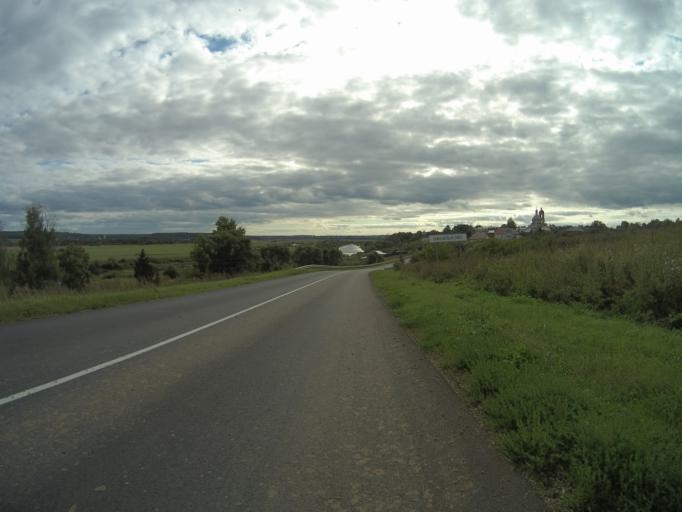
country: RU
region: Vladimir
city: Bogolyubovo
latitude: 56.2998
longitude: 40.5753
